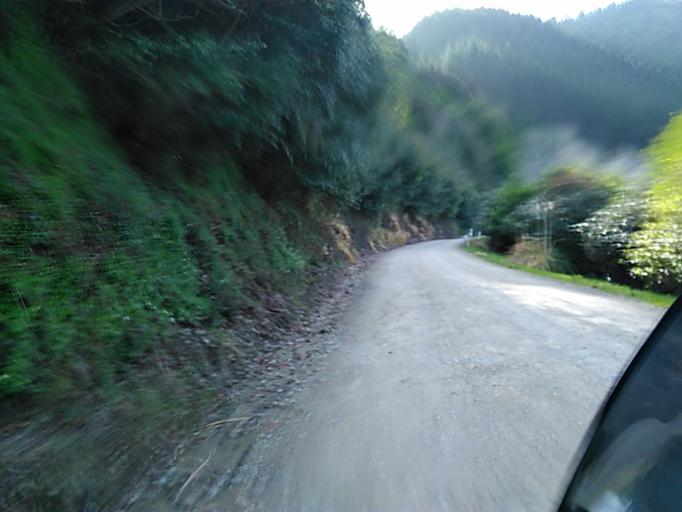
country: NZ
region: Gisborne
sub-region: Gisborne District
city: Gisborne
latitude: -38.6260
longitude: 178.0520
